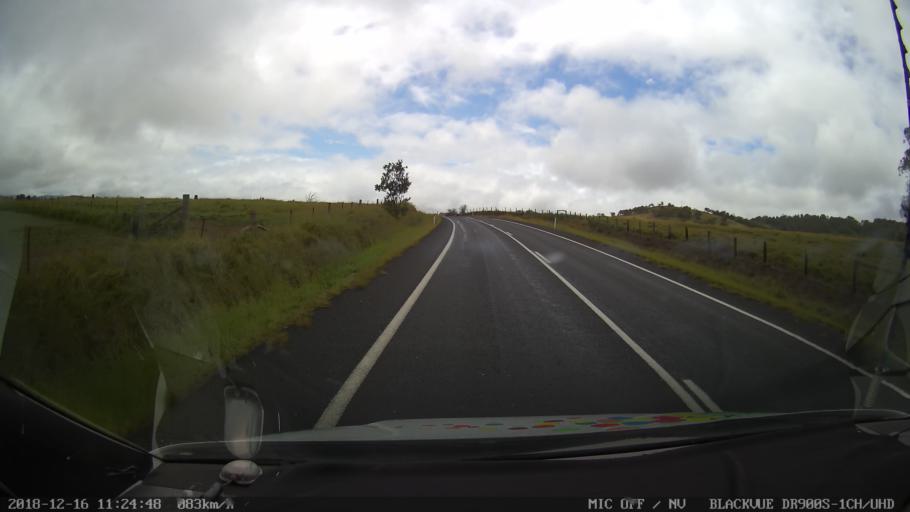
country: AU
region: New South Wales
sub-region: Tenterfield Municipality
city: Carrolls Creek
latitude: -29.0583
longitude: 152.0532
